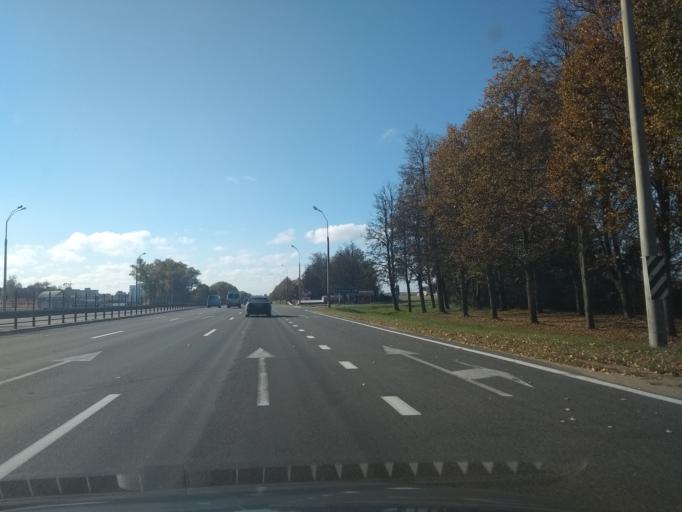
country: BY
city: Fanipol
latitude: 53.7532
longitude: 27.3271
